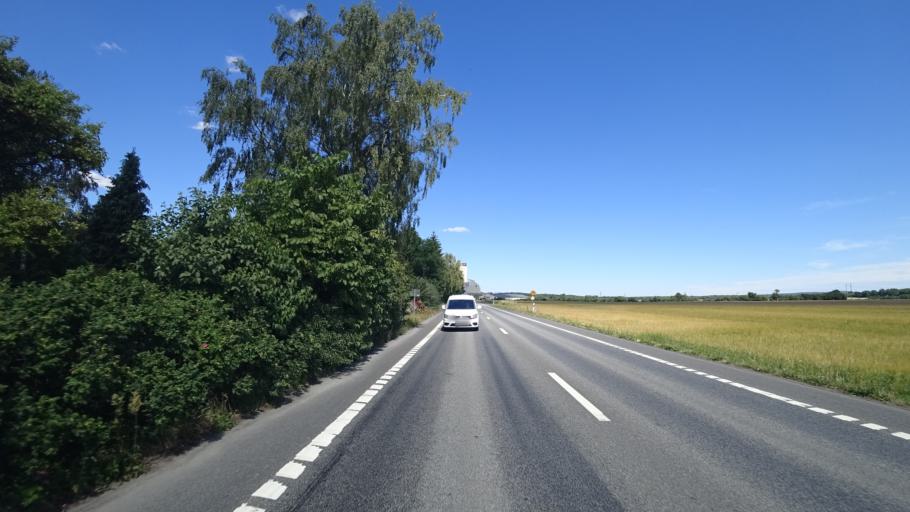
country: SE
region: Skane
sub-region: Kristianstads Kommun
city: Kristianstad
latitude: 56.0349
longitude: 14.0958
